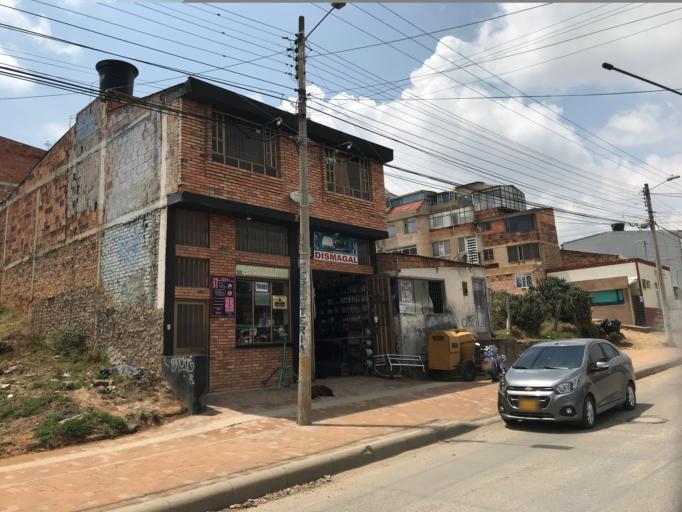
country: CO
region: Boyaca
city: Tunja
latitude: 5.5430
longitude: -73.3679
